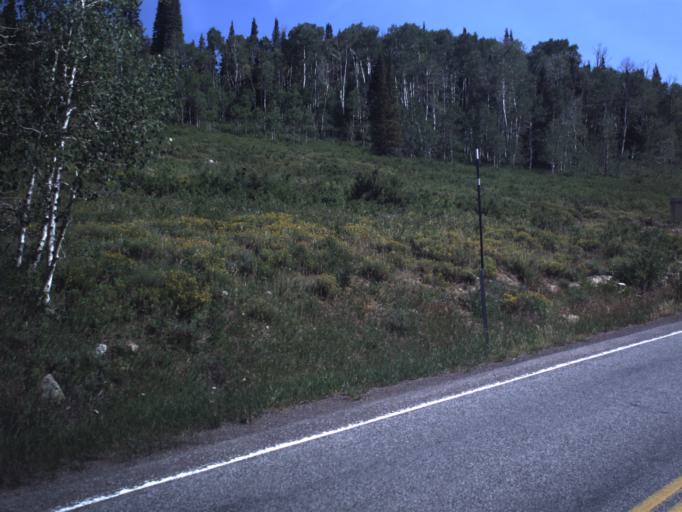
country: US
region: Utah
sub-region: Sanpete County
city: Fairview
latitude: 39.6764
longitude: -111.3280
